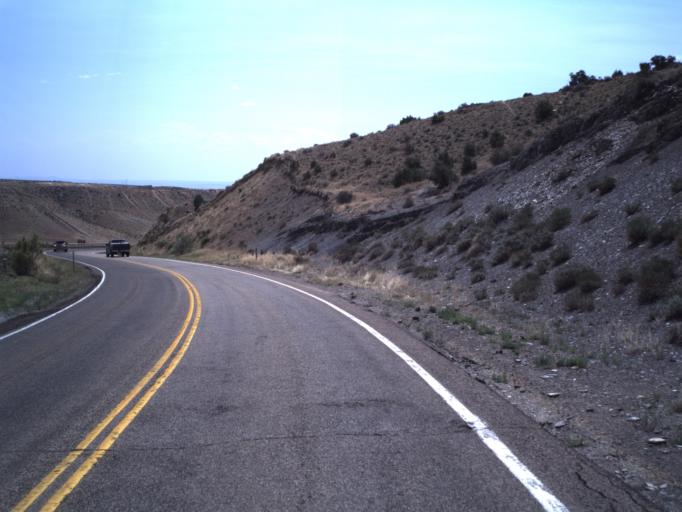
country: US
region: Utah
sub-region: Uintah County
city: Vernal
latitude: 40.5130
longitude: -109.5259
